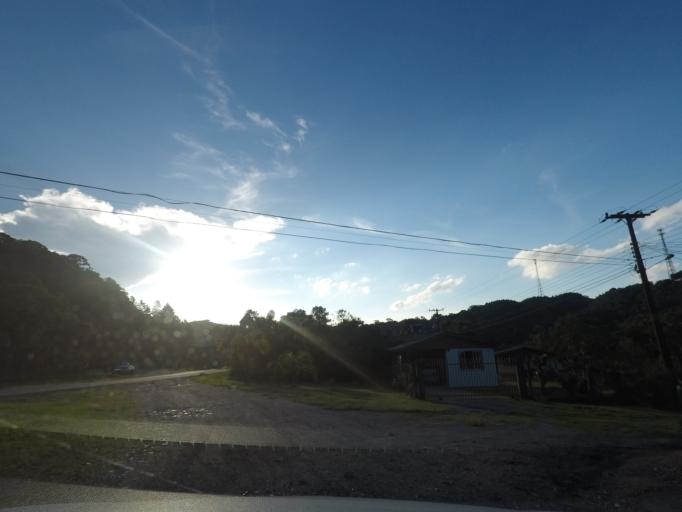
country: BR
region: Parana
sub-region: Campina Grande Do Sul
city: Campina Grande do Sul
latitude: -25.3066
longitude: -48.9443
